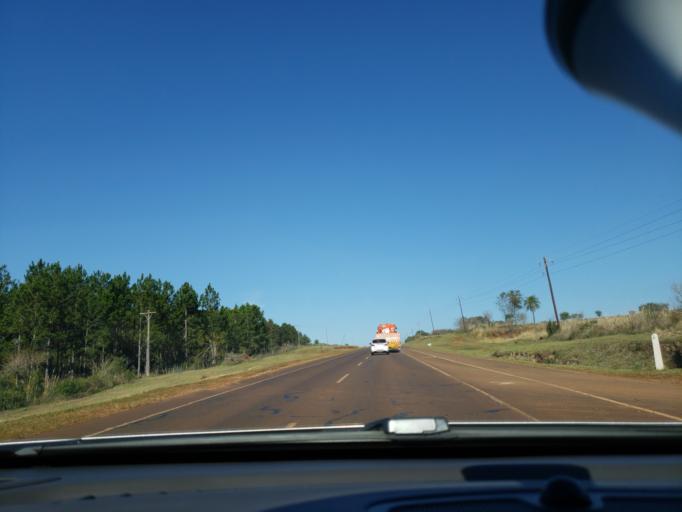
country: AR
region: Misiones
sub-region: Departamento de Apostoles
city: San Jose
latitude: -27.7536
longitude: -55.7768
